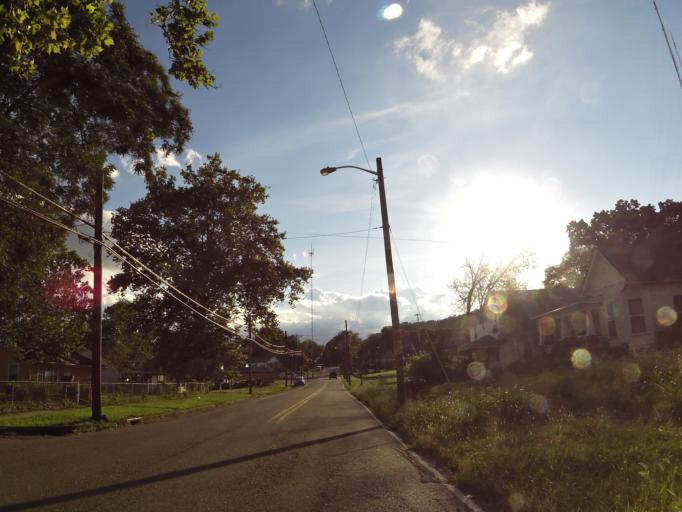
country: US
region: Tennessee
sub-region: Knox County
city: Knoxville
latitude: 36.0002
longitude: -83.9357
